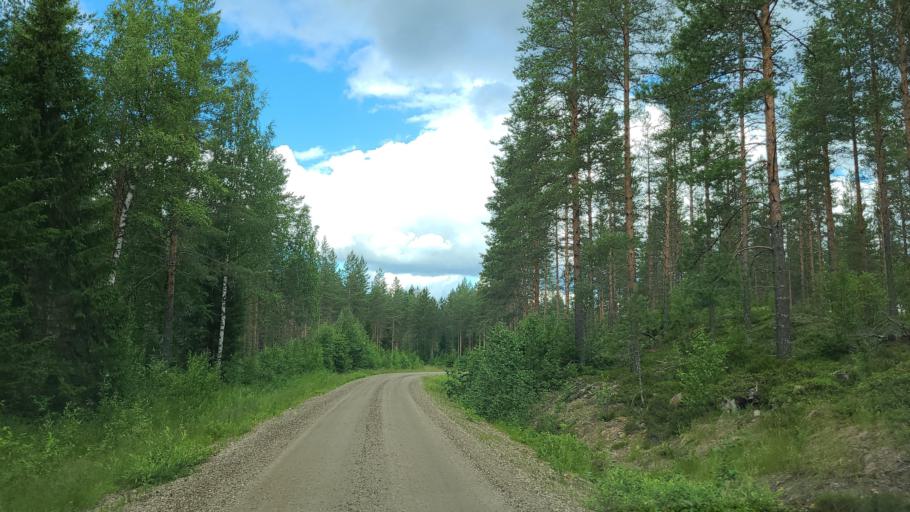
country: FI
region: Northern Savo
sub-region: Koillis-Savo
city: Kaavi
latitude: 63.0318
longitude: 28.7850
